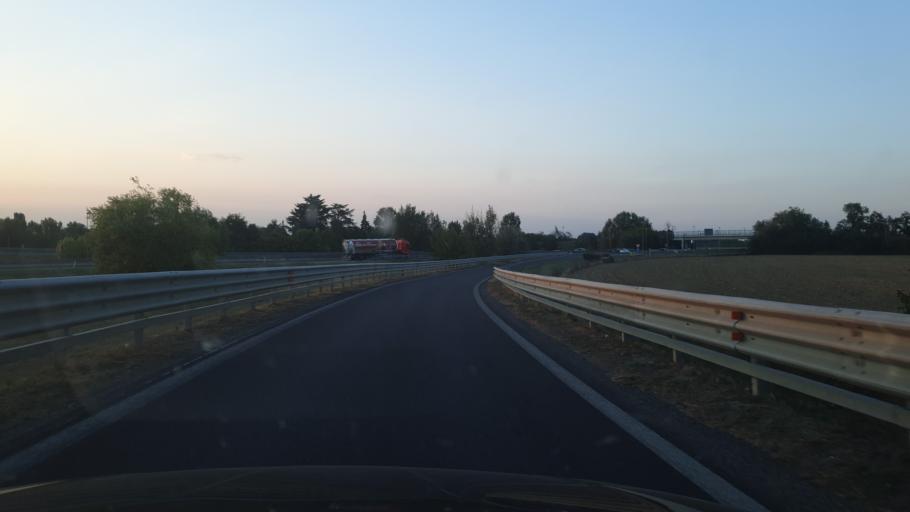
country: IT
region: Emilia-Romagna
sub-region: Provincia di Bologna
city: Castel Maggiore
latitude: 44.5906
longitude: 11.4011
